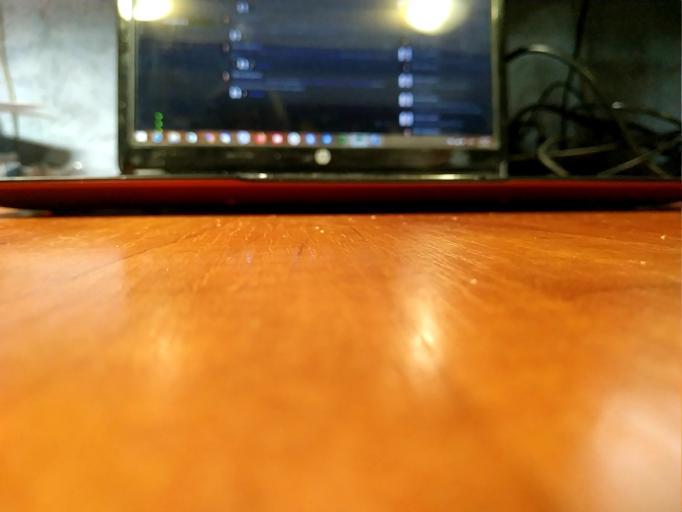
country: RU
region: Tverskaya
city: Sandovo
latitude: 58.4674
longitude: 36.4004
